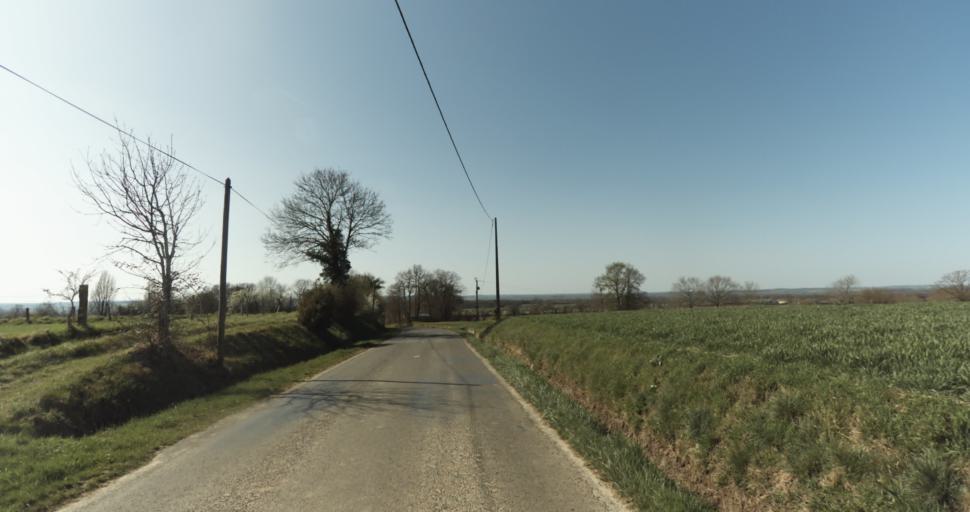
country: FR
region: Lower Normandy
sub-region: Departement du Calvados
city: Saint-Pierre-sur-Dives
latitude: 48.9403
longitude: -0.0113
